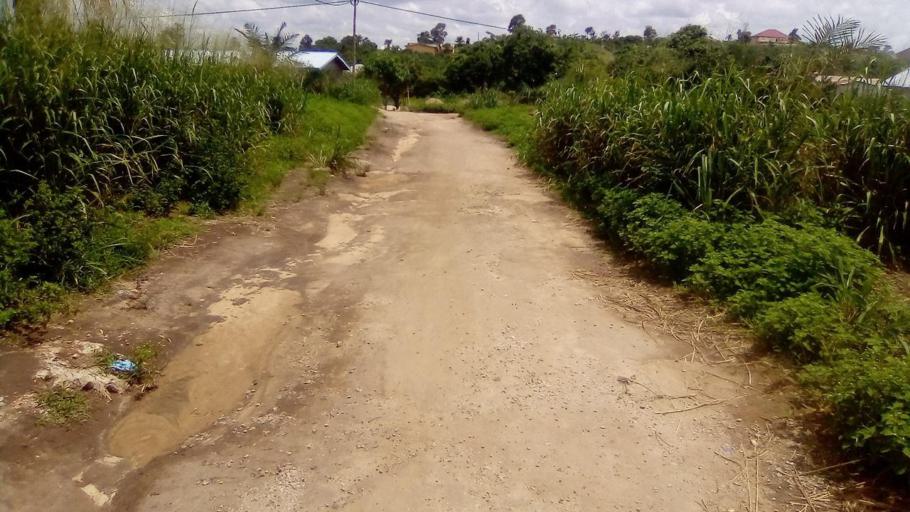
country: SL
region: Southern Province
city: Bo
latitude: 7.9350
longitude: -11.7482
